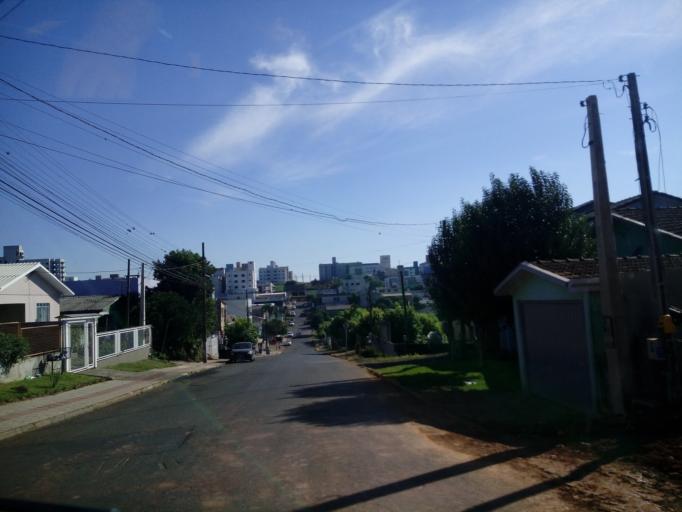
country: BR
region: Santa Catarina
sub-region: Chapeco
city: Chapeco
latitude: -27.0989
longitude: -52.6696
